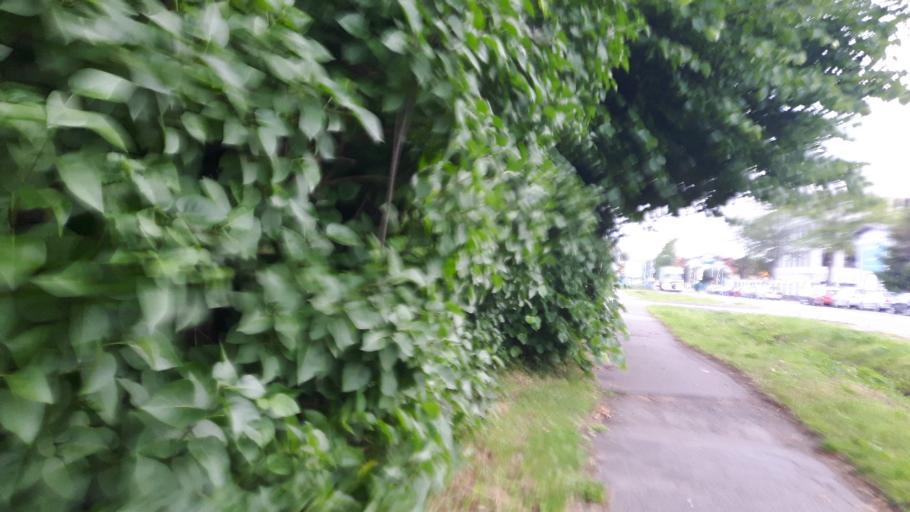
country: PL
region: West Pomeranian Voivodeship
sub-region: Powiat policki
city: Przeclaw
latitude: 53.3967
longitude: 14.4925
